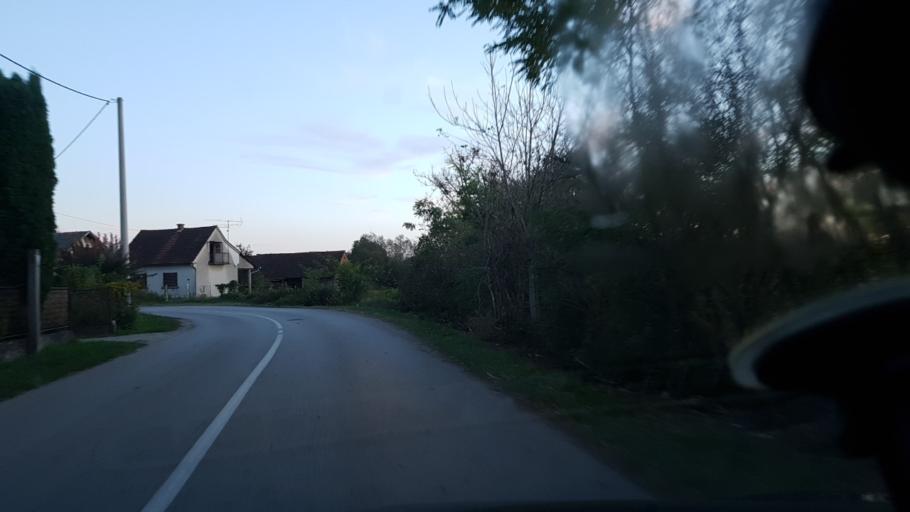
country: HR
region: Zagrebacka
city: Bregana
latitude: 45.8676
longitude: 15.7124
